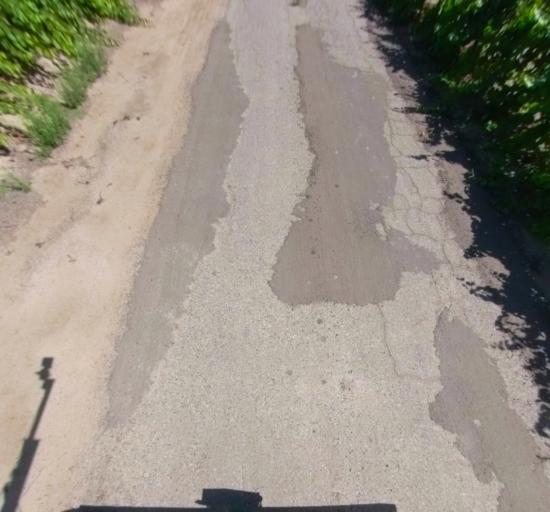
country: US
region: California
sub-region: Madera County
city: Madera
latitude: 36.9496
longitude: -120.1749
